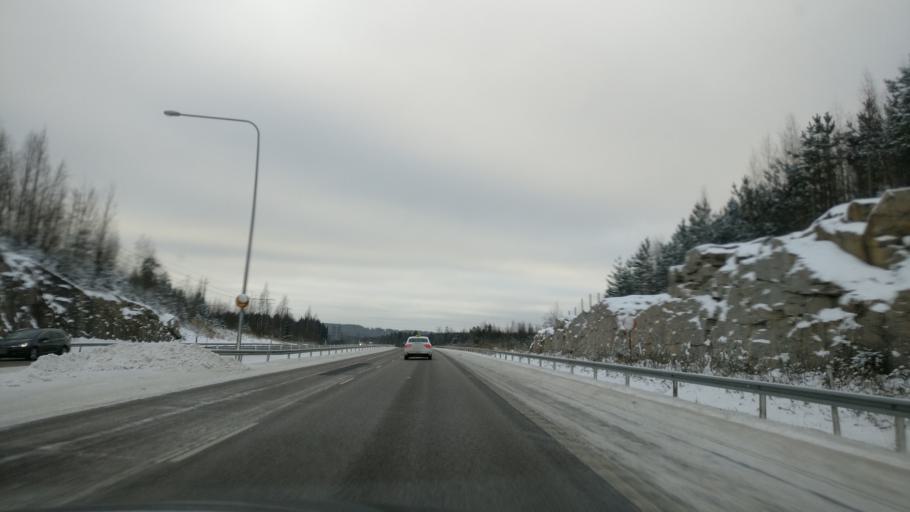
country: FI
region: Paijanne Tavastia
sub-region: Lahti
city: Lahti
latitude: 60.9636
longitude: 25.7061
